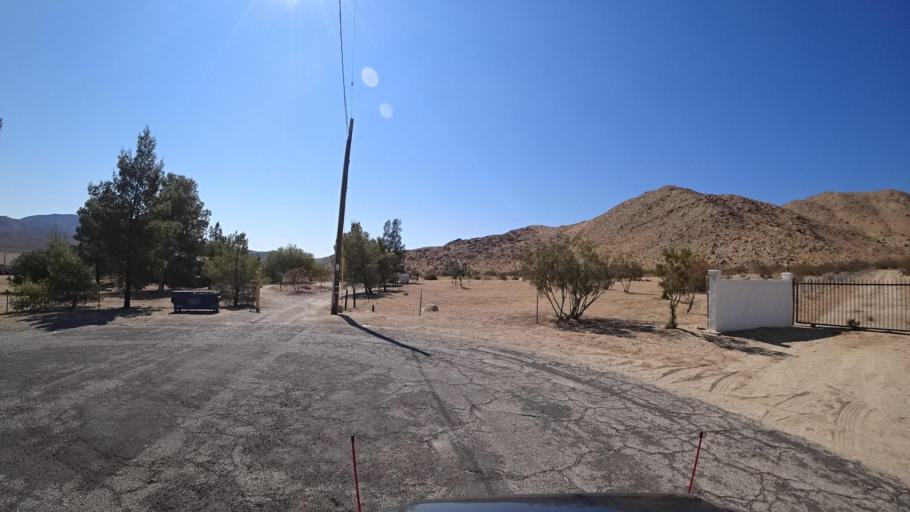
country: US
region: California
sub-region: San Diego County
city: Julian
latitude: 33.0652
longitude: -116.4380
